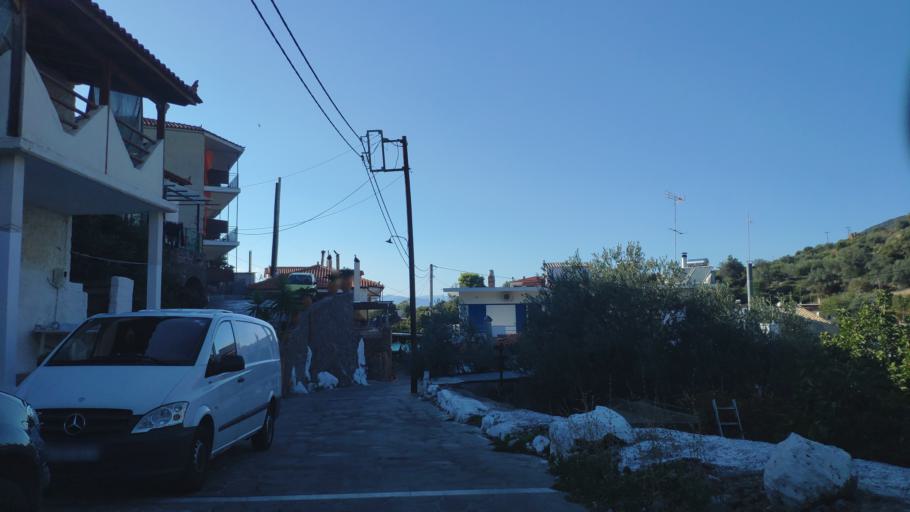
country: GR
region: Attica
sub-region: Nomos Piraios
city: Megalochori
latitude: 37.5931
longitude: 23.3403
